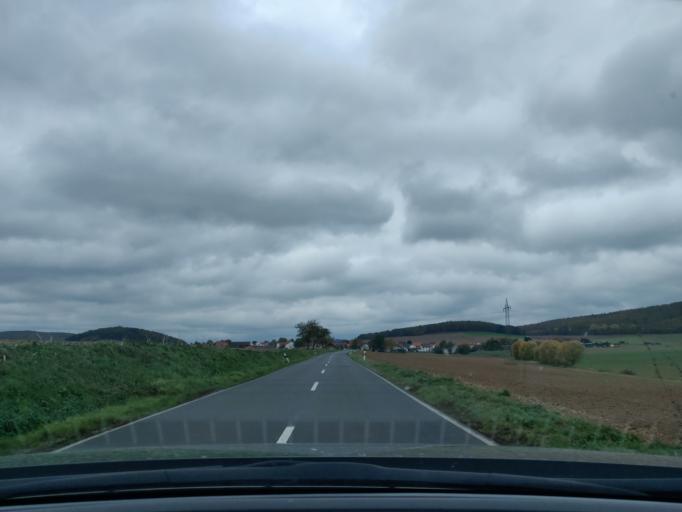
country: DE
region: Hesse
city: Fritzlar
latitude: 51.1833
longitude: 9.2822
